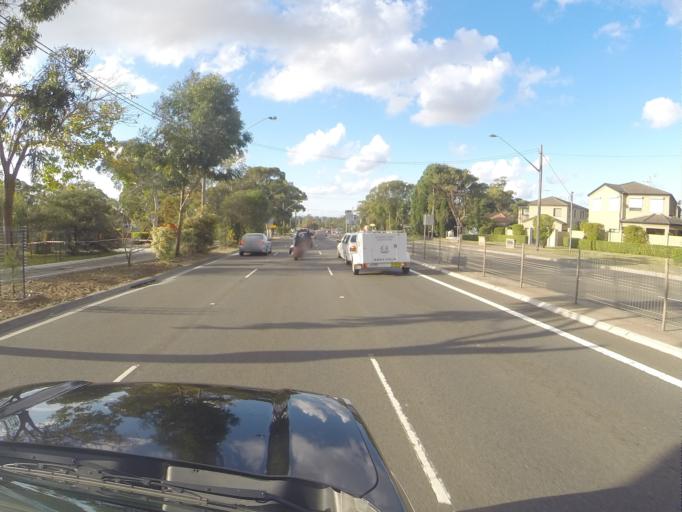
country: AU
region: New South Wales
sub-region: Sutherland Shire
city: Gymea
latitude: -34.0283
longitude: 151.0826
